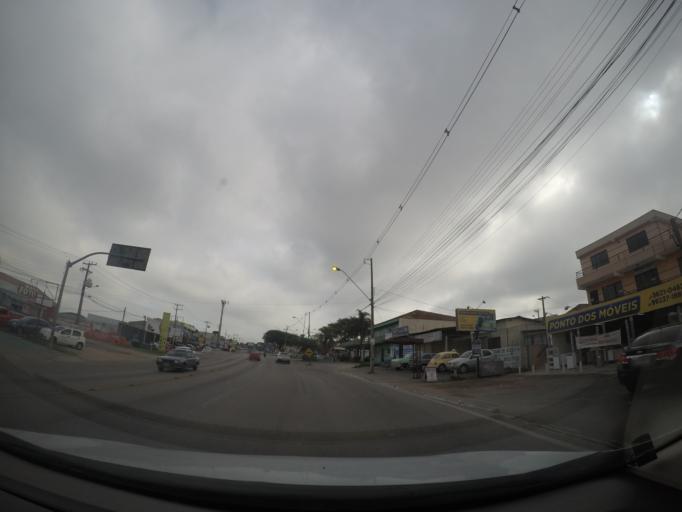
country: BR
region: Parana
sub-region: Colombo
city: Colombo
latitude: -25.3534
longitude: -49.2190
